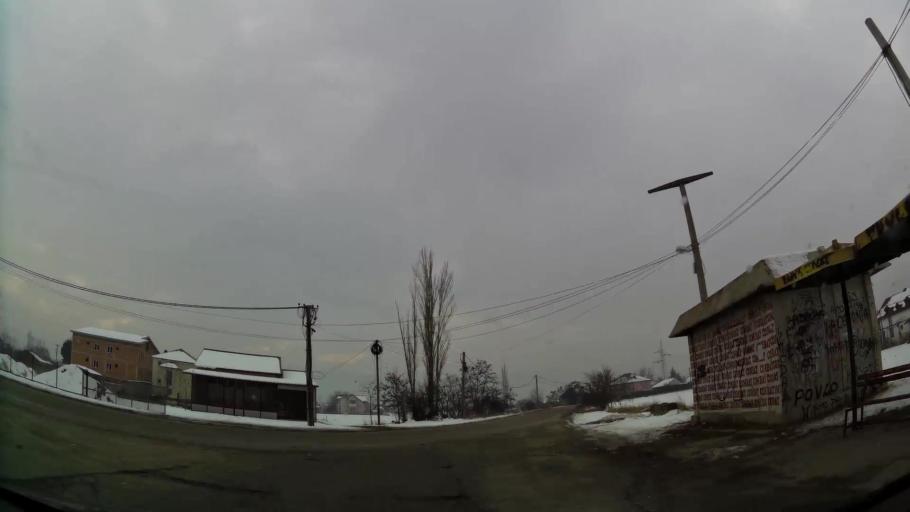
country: MK
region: Saraj
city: Saraj
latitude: 42.0448
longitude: 21.3576
